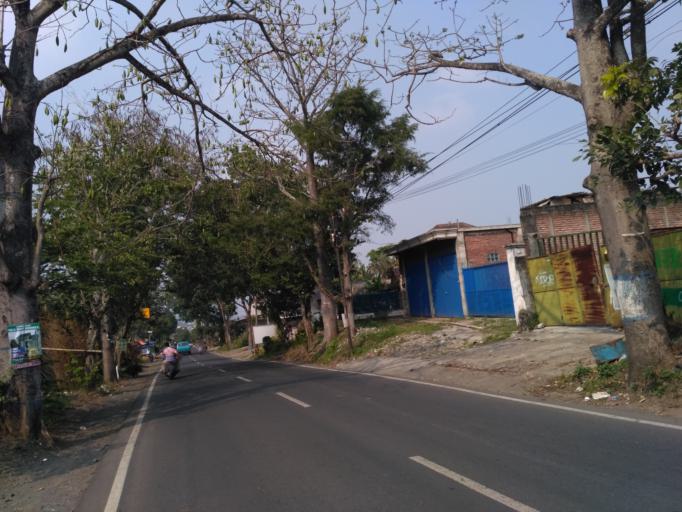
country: ID
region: East Java
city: Batu
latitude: -7.8647
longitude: 112.5427
